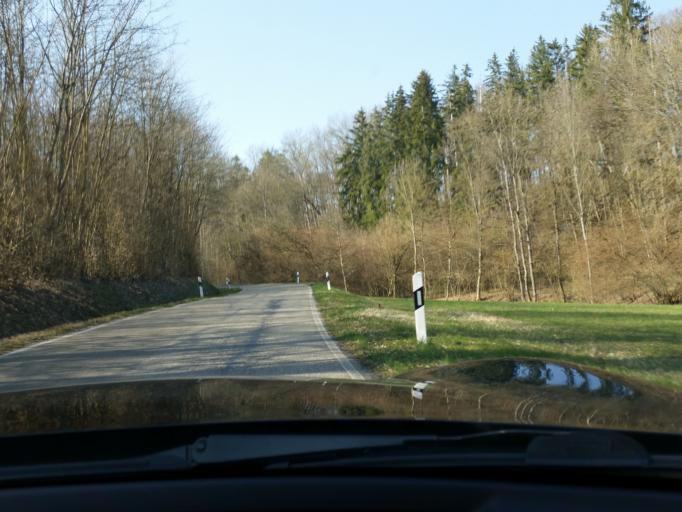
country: DE
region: Baden-Wuerttemberg
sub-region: Regierungsbezirk Stuttgart
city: Jagsthausen
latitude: 49.3594
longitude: 9.4684
